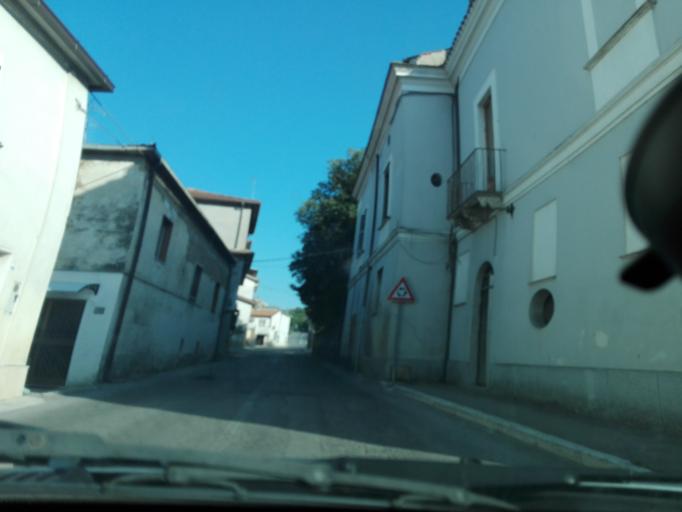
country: IT
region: Abruzzo
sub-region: Provincia di Pescara
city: Cappelle sul Tavo
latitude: 42.4634
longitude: 14.1042
